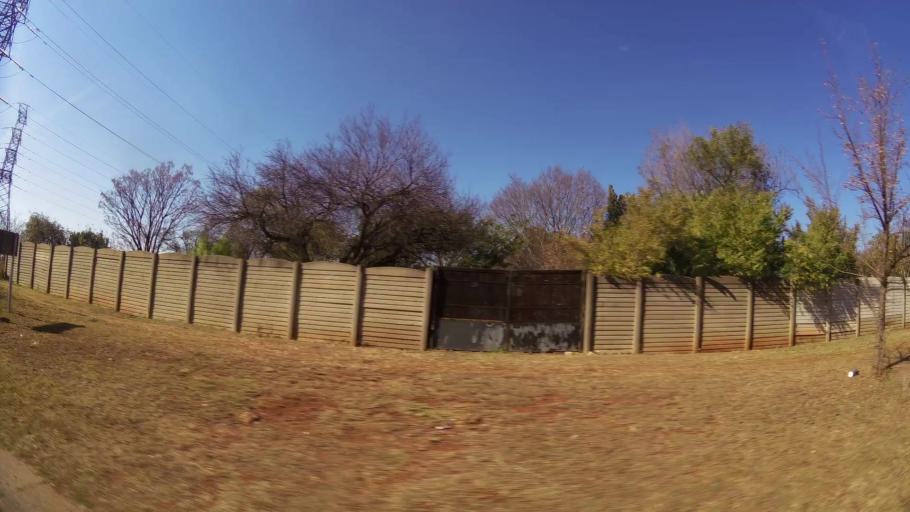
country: ZA
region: Gauteng
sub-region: City of Tshwane Metropolitan Municipality
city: Centurion
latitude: -25.8326
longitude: 28.1716
